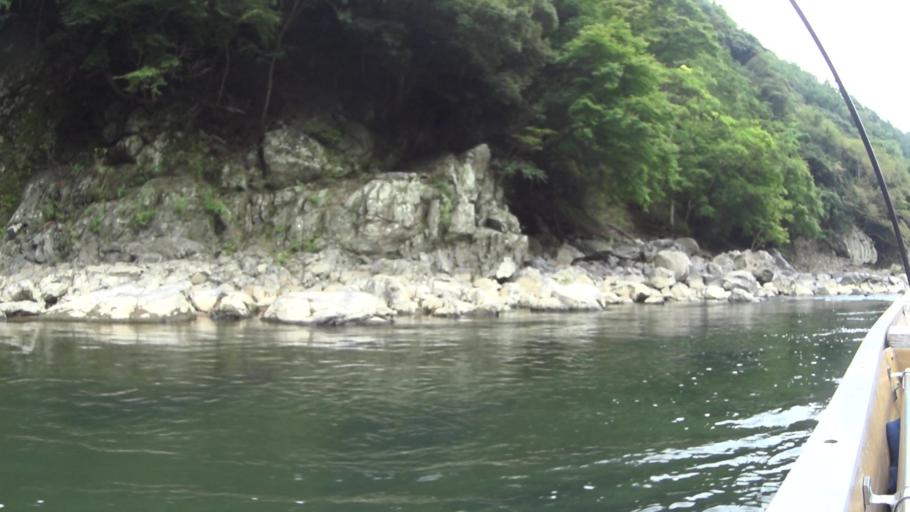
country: JP
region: Kyoto
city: Kameoka
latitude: 35.0180
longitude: 135.6105
